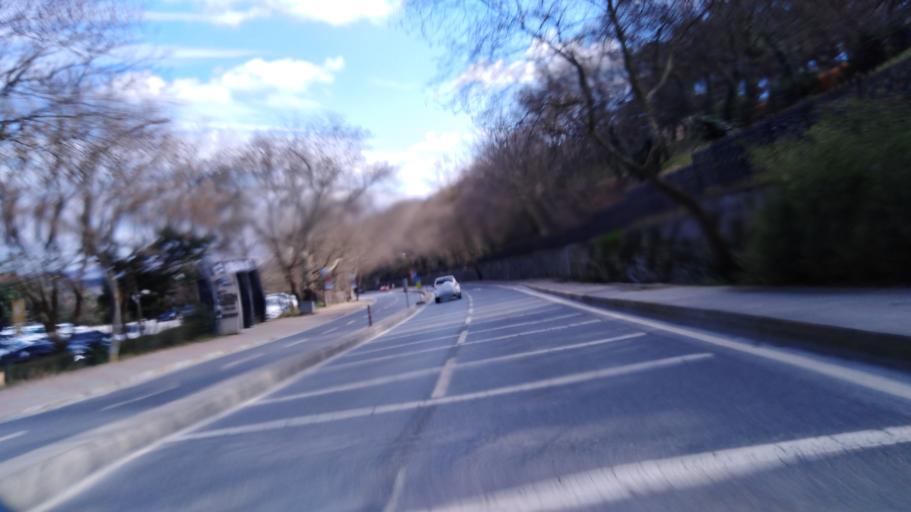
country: TR
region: Istanbul
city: Sisli
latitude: 41.1105
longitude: 29.0498
